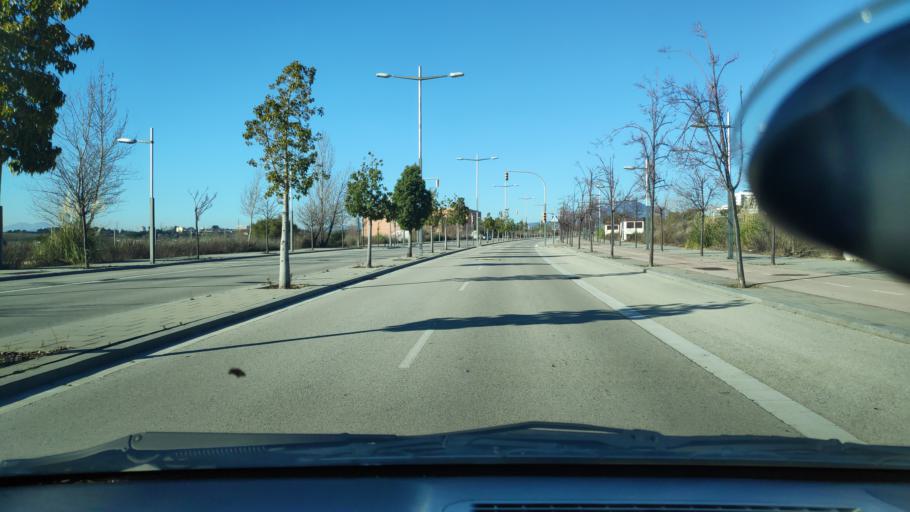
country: ES
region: Catalonia
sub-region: Provincia de Barcelona
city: Sant Quirze del Valles
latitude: 41.5438
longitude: 2.0814
